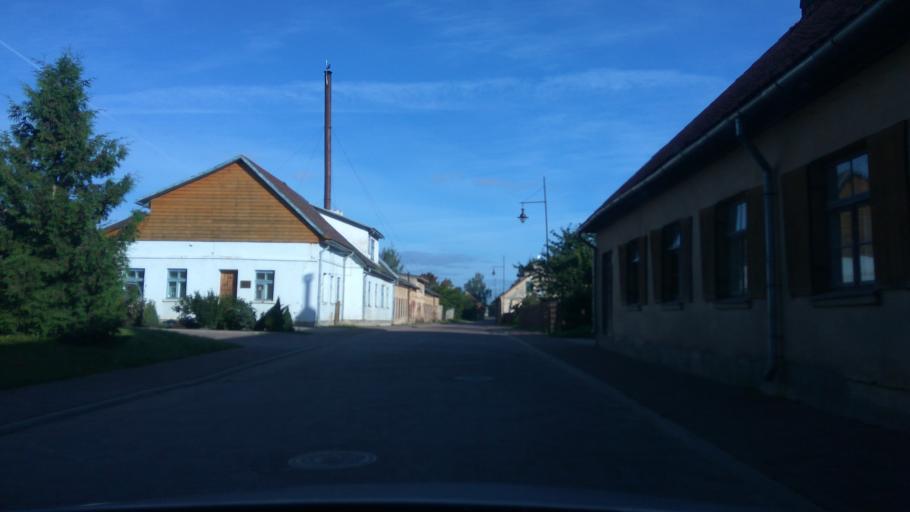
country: LV
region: Kuldigas Rajons
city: Kuldiga
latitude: 56.9720
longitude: 21.9711
